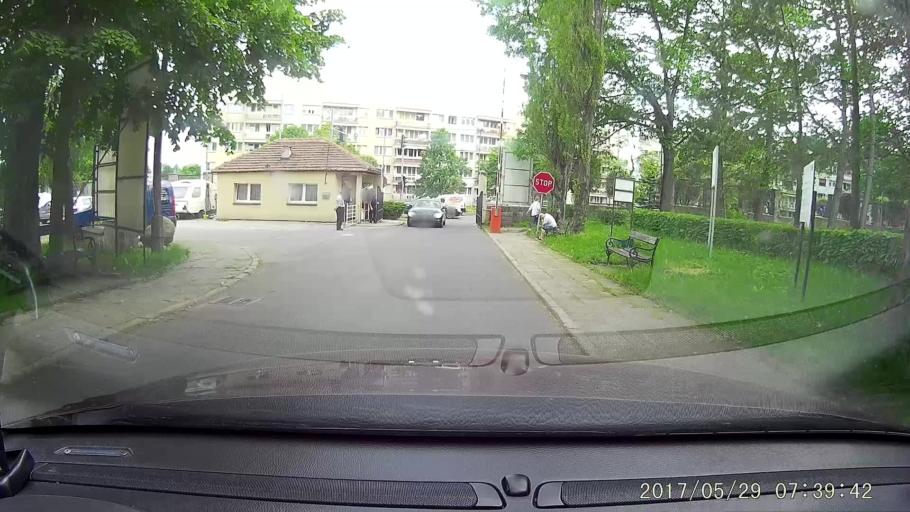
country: PL
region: Lower Silesian Voivodeship
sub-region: Powiat boleslawiecki
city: Boleslawiec
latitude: 51.2603
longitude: 15.5834
